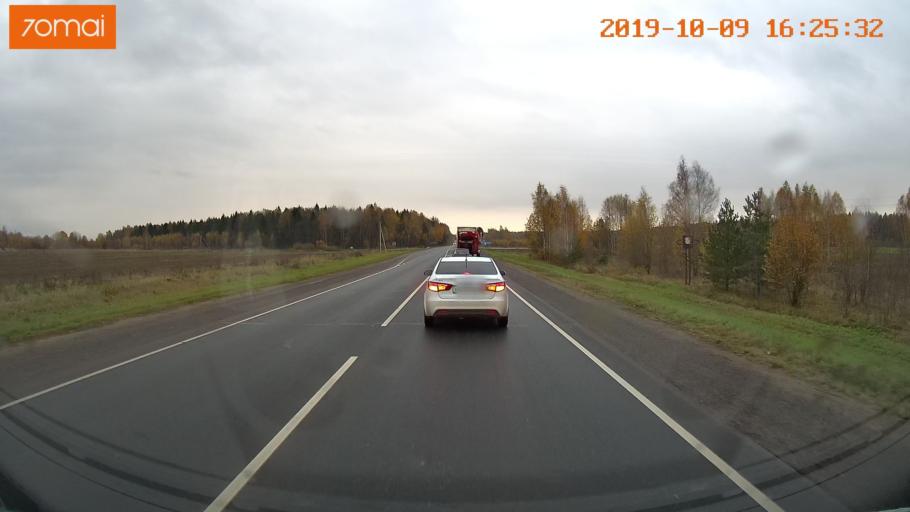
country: RU
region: Kostroma
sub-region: Kostromskoy Rayon
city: Kostroma
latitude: 57.6419
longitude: 40.9202
